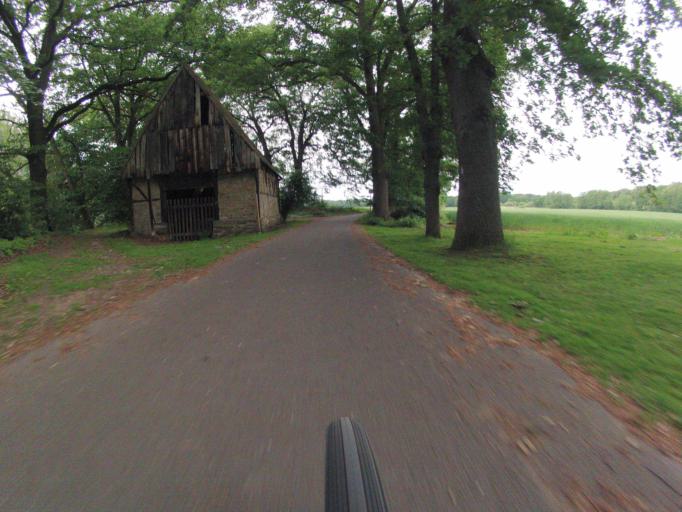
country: DE
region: North Rhine-Westphalia
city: Emsdetten
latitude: 52.2207
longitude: 7.5223
